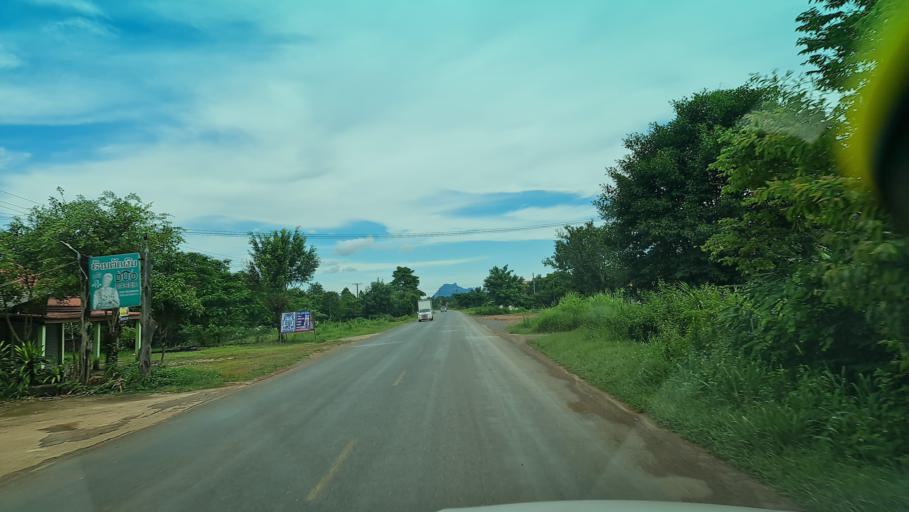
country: LA
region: Bolikhamxai
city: Ban Nahin
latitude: 18.1148
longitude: 104.2734
